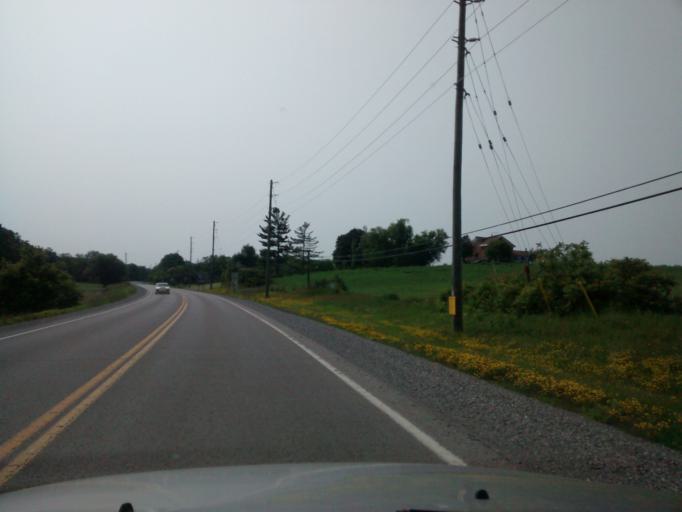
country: CA
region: Ontario
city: Ancaster
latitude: 43.0633
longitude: -79.9242
